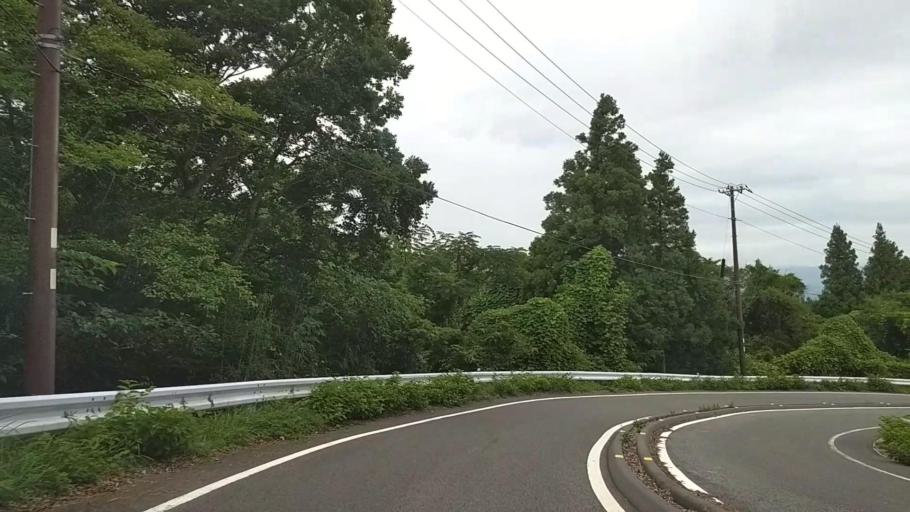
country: JP
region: Shizuoka
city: Gotemba
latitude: 35.3231
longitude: 139.0085
